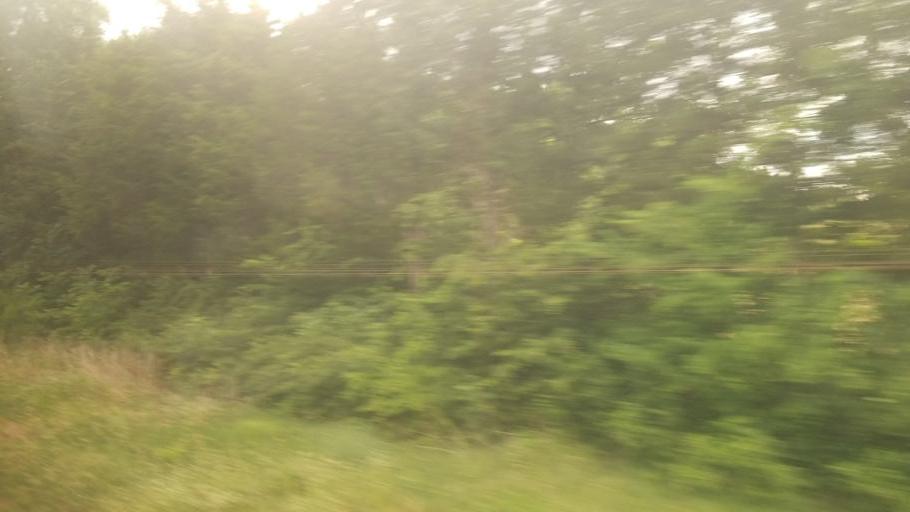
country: US
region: Kansas
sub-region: Osage County
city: Carbondale
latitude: 38.8794
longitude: -95.6910
